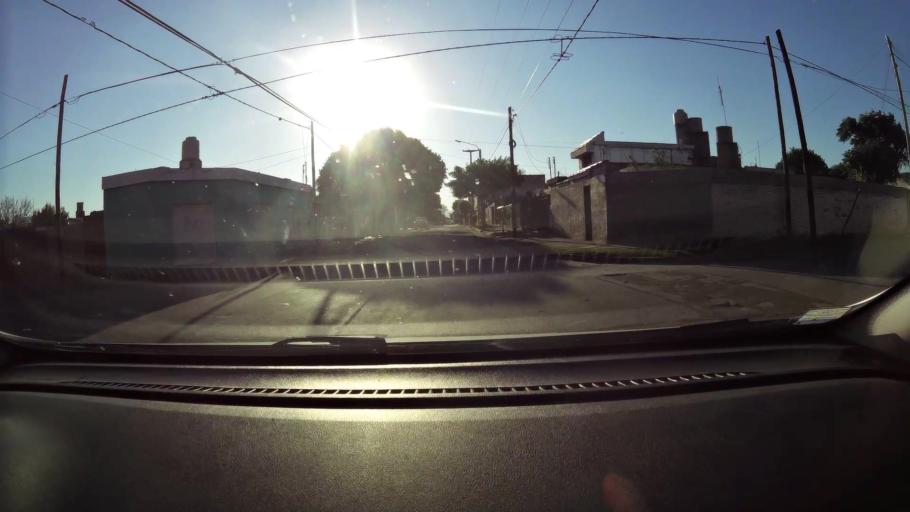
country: AR
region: Cordoba
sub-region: Departamento de Capital
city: Cordoba
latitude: -31.3751
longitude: -64.1923
